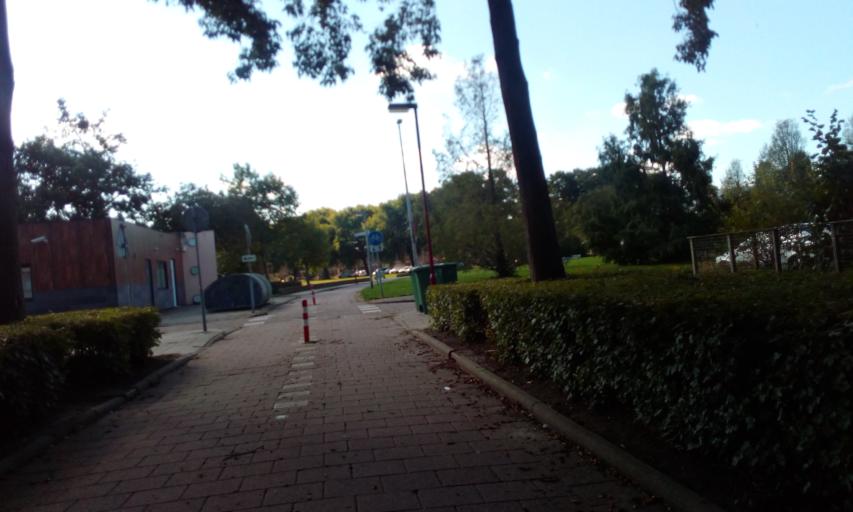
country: NL
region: South Holland
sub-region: Gemeente Rijnwoude
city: Benthuizen
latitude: 52.0754
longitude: 4.5183
